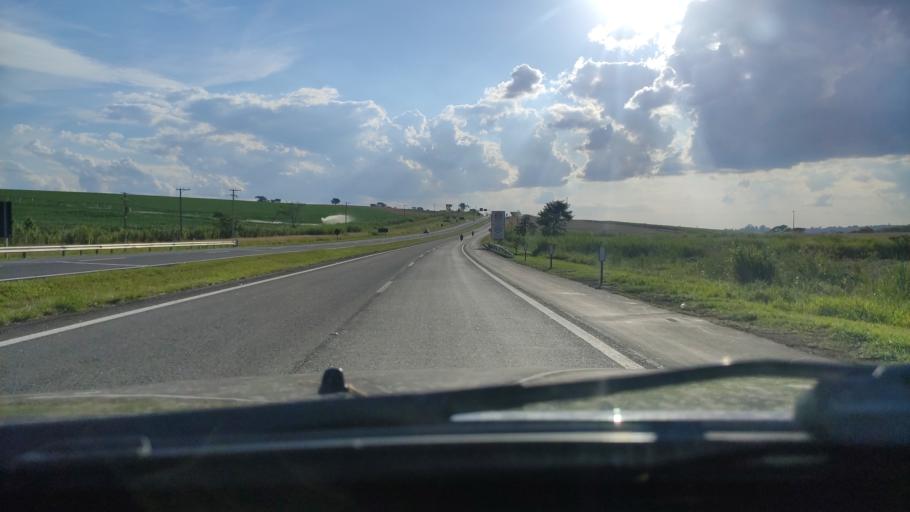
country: BR
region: Sao Paulo
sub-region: Mogi-Mirim
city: Mogi Mirim
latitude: -22.4568
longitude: -46.9056
